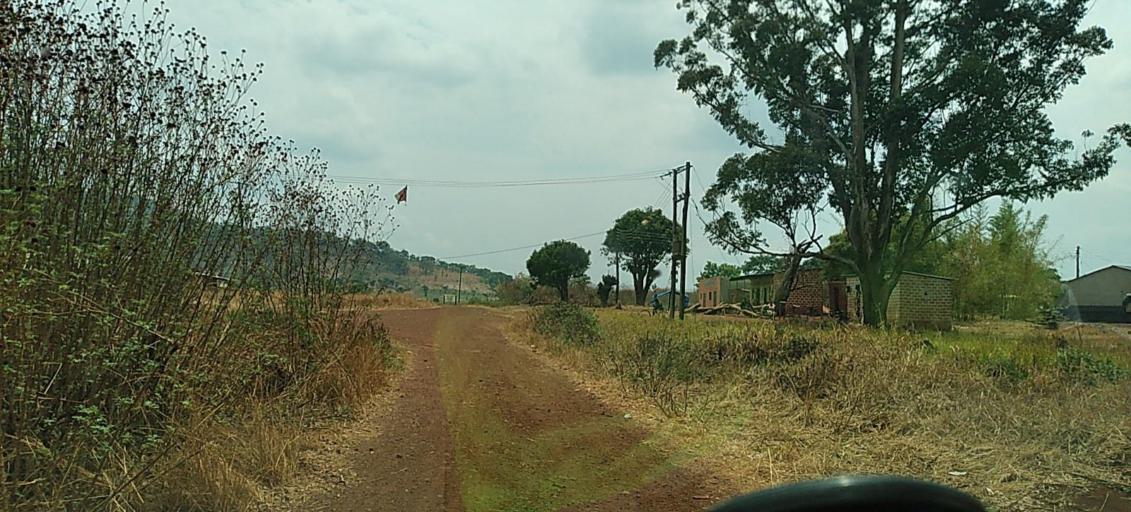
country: ZM
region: North-Western
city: Kansanshi
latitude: -12.0309
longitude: 26.4355
